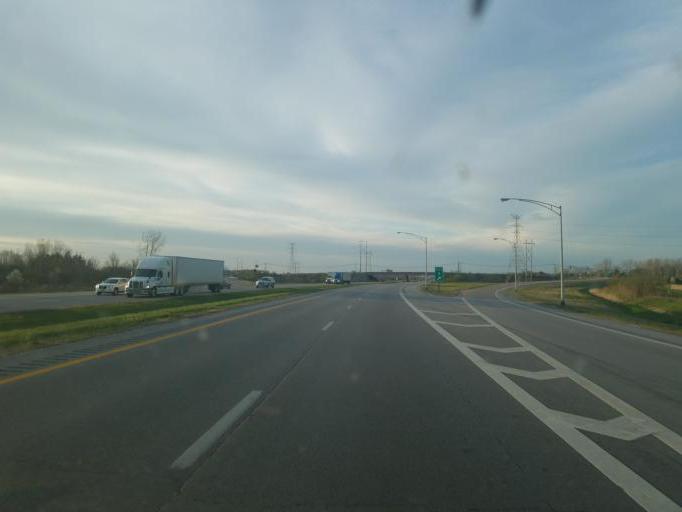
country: US
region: Ohio
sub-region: Wood County
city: Walbridge
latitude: 41.5843
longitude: -83.4766
